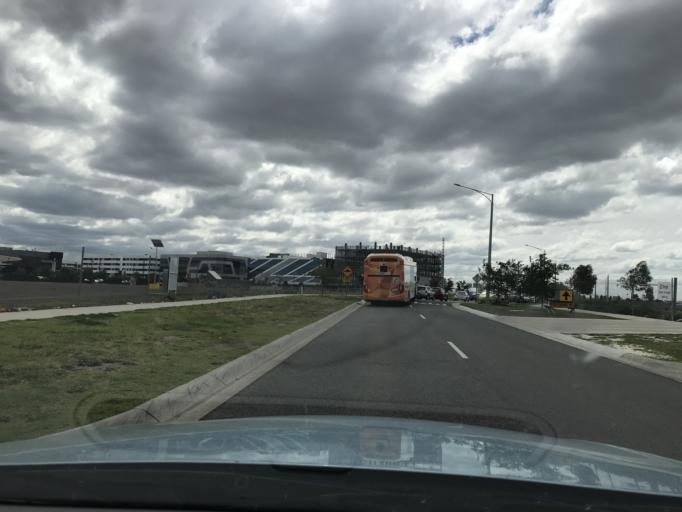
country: AU
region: Victoria
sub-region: Wyndham
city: Williams Landing
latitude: -37.8691
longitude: 144.7461
